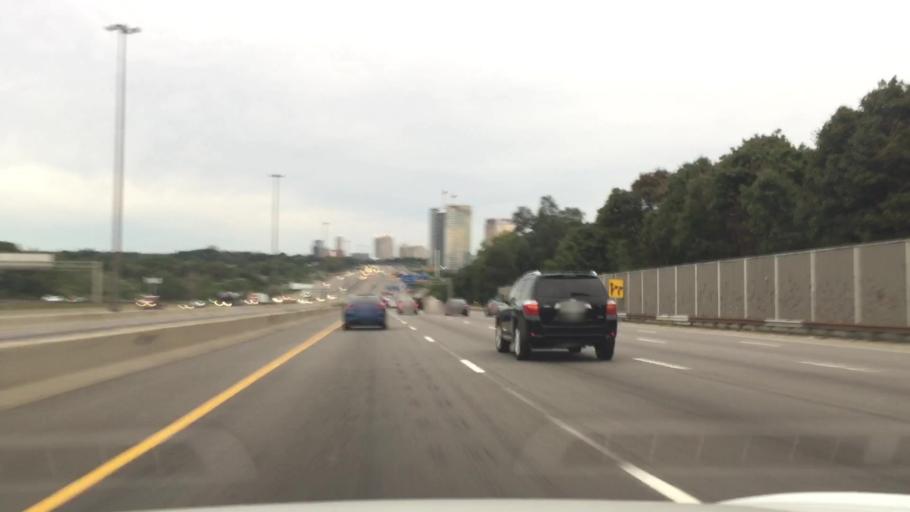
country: CA
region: Ontario
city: Willowdale
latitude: 43.7655
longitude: -79.3506
